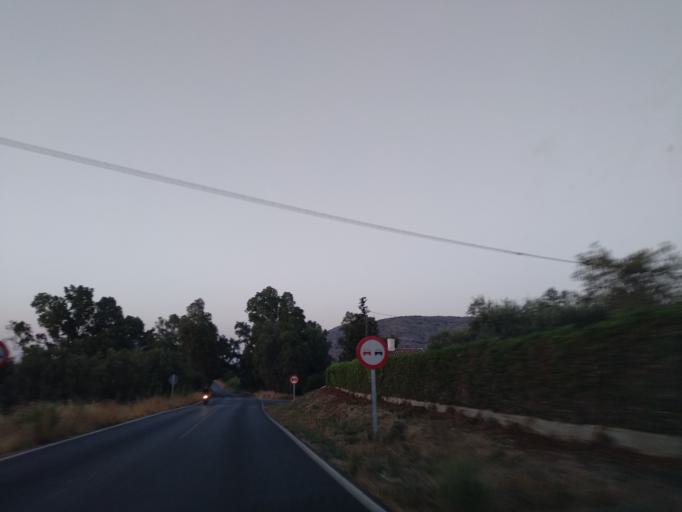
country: ES
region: Andalusia
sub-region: Provincia de Malaga
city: Cartama
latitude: 36.6814
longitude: -4.6565
